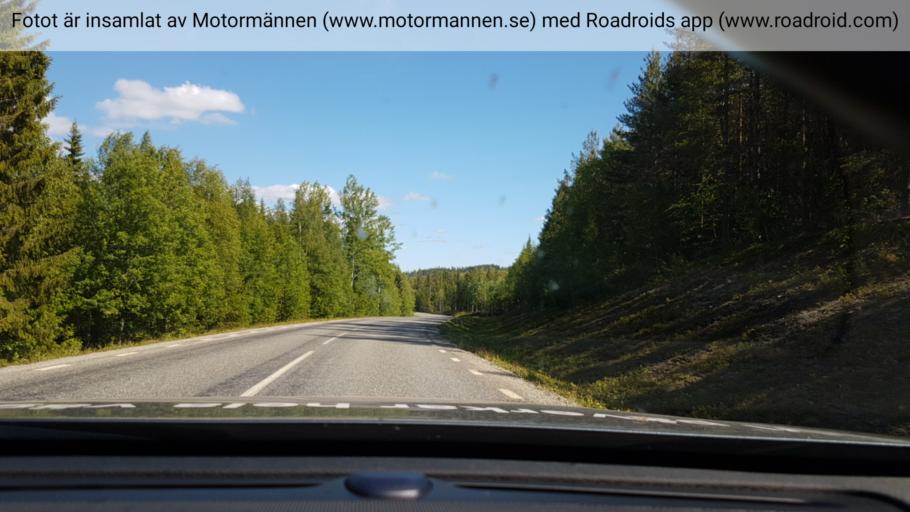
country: SE
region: Vaesterbotten
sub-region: Lycksele Kommun
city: Lycksele
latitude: 64.6249
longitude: 18.3853
